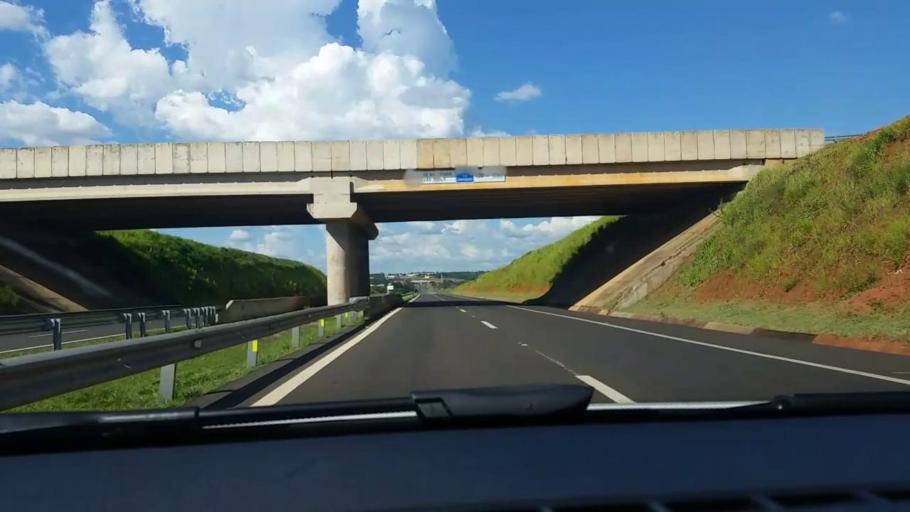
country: BR
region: Sao Paulo
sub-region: Bauru
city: Bauru
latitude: -22.3774
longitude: -49.0605
